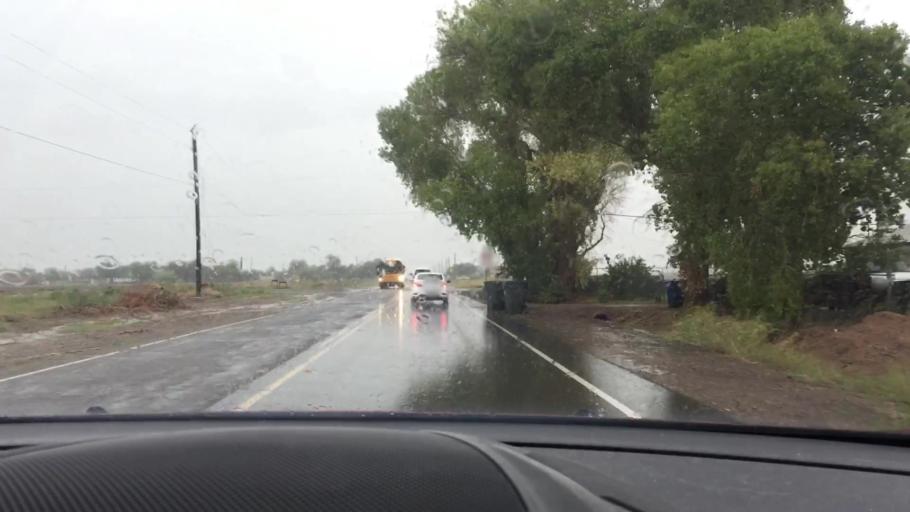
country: US
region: Arizona
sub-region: Maricopa County
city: Scottsdale
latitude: 33.4725
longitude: -111.8827
